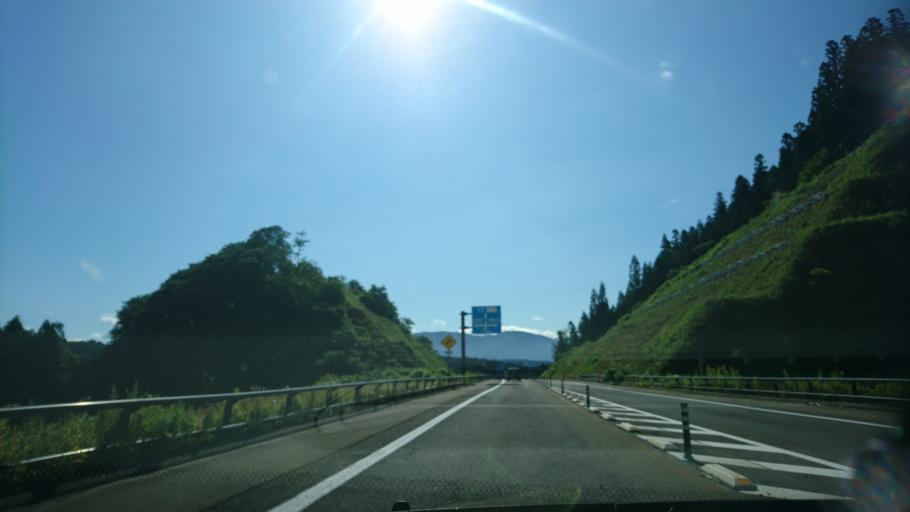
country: JP
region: Akita
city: Kakunodatemachi
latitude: 39.5954
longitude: 140.5322
